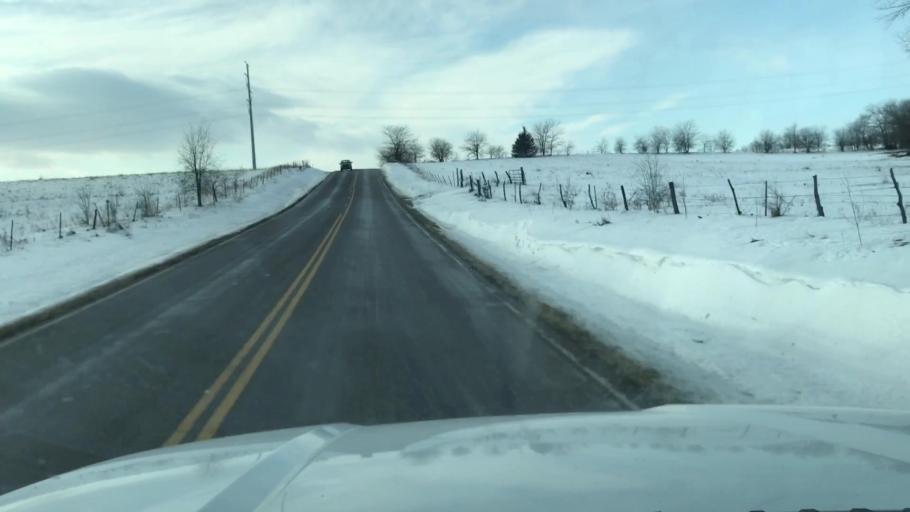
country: US
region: Missouri
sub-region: Nodaway County
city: Maryville
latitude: 40.2004
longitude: -94.8741
